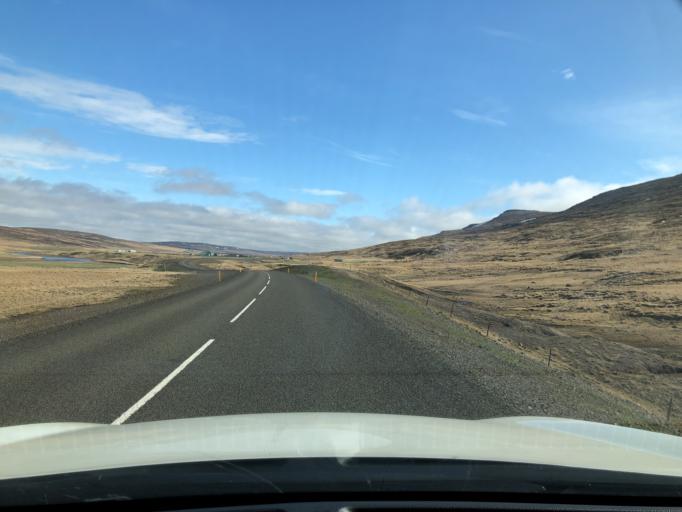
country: IS
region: West
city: Borgarnes
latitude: 65.1579
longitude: -21.5395
